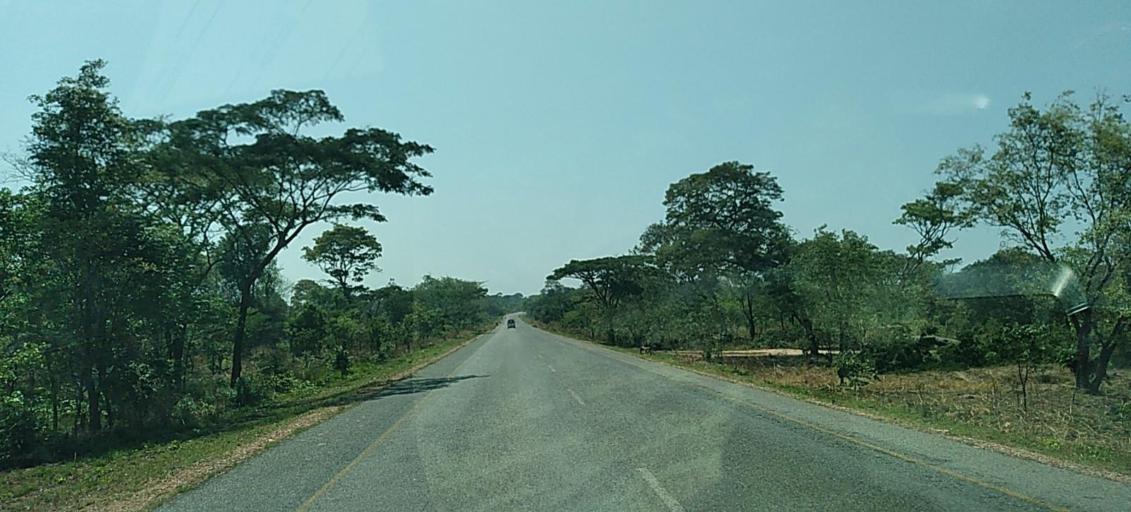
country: ZM
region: North-Western
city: Solwezi
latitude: -12.2845
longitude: 25.7807
